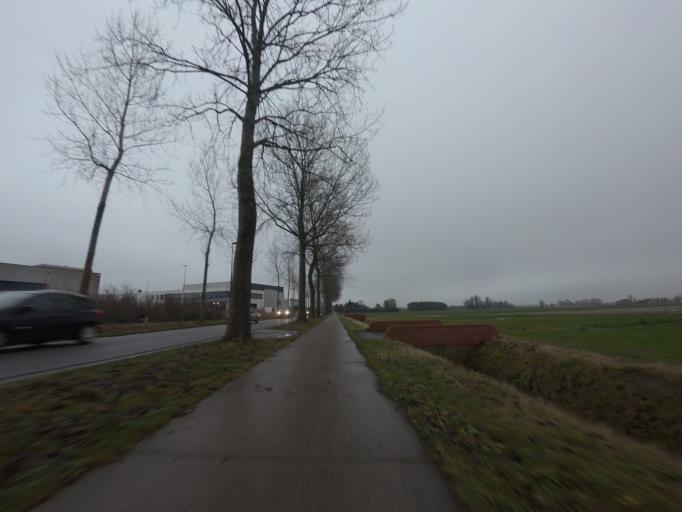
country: BE
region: Flanders
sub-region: Provincie West-Vlaanderen
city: Knokke-Heist
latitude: 51.3175
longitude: 3.2913
